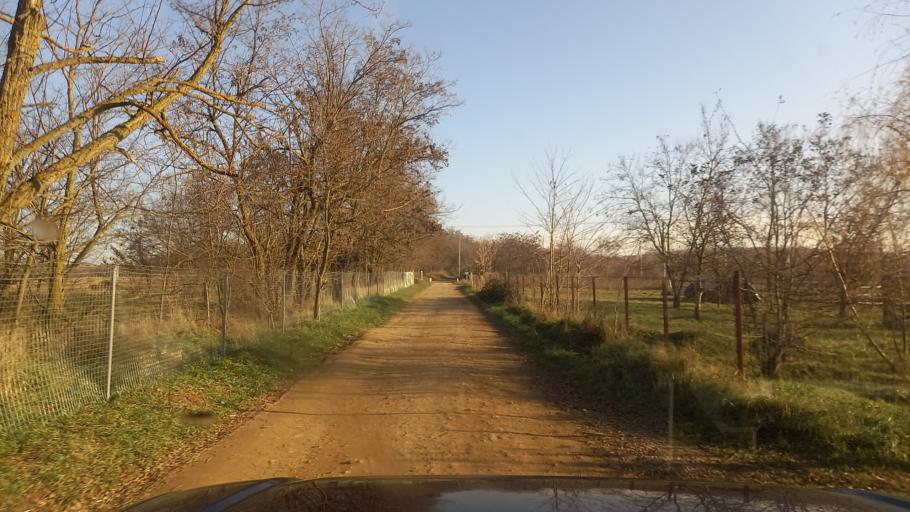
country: RU
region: Krasnodarskiy
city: Il'skiy
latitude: 44.8096
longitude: 38.5865
